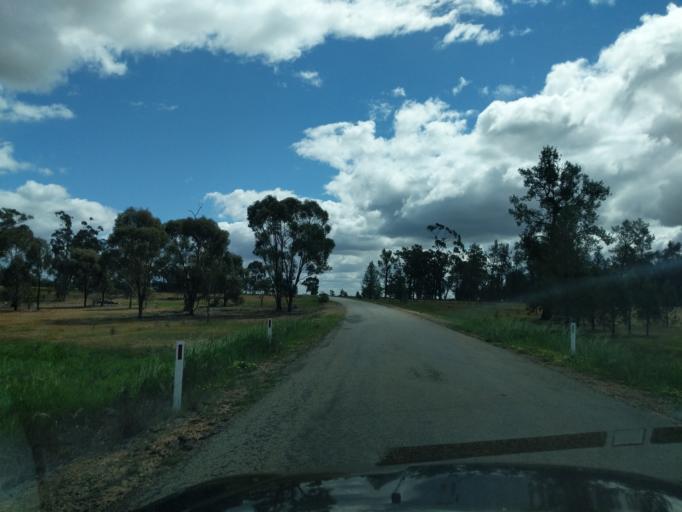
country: AU
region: New South Wales
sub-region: Coolamon
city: Coolamon
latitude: -34.8707
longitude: 146.9007
